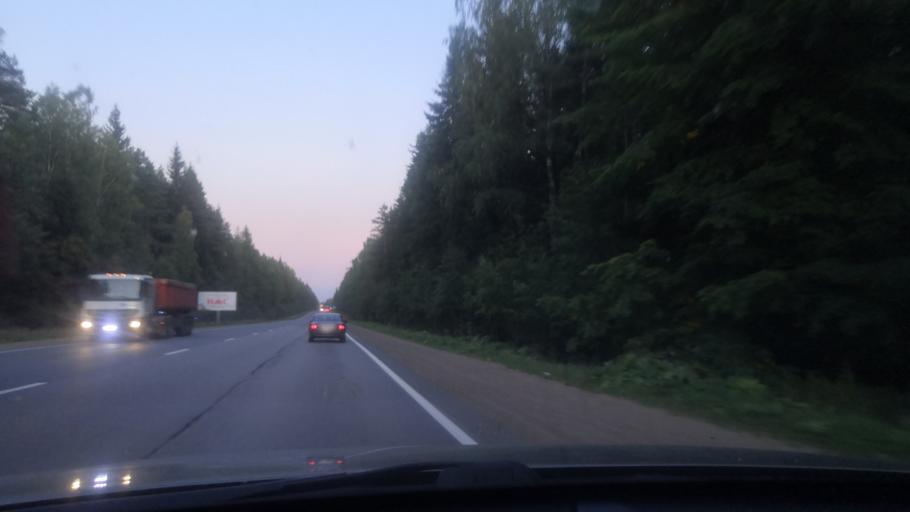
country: RU
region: St.-Petersburg
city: Pesochnyy
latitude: 60.1863
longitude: 30.1108
